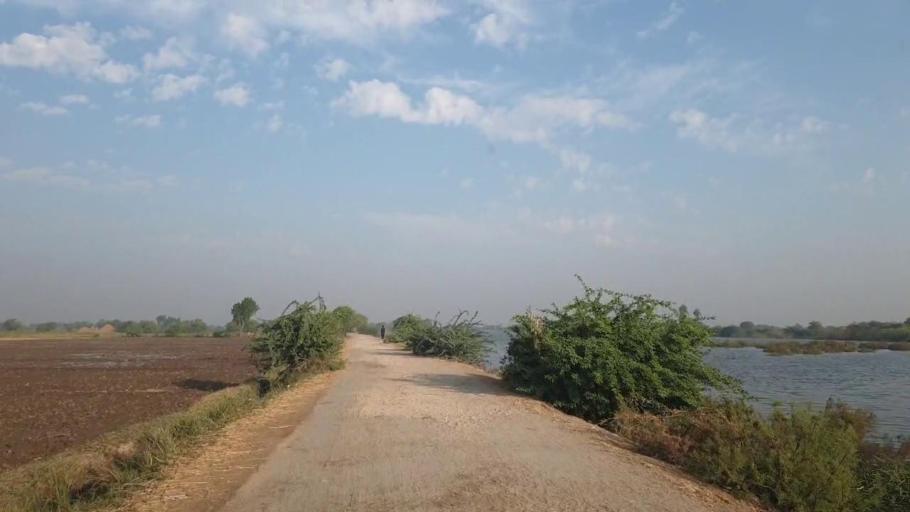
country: PK
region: Sindh
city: Tando Bago
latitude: 24.7971
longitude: 68.9612
